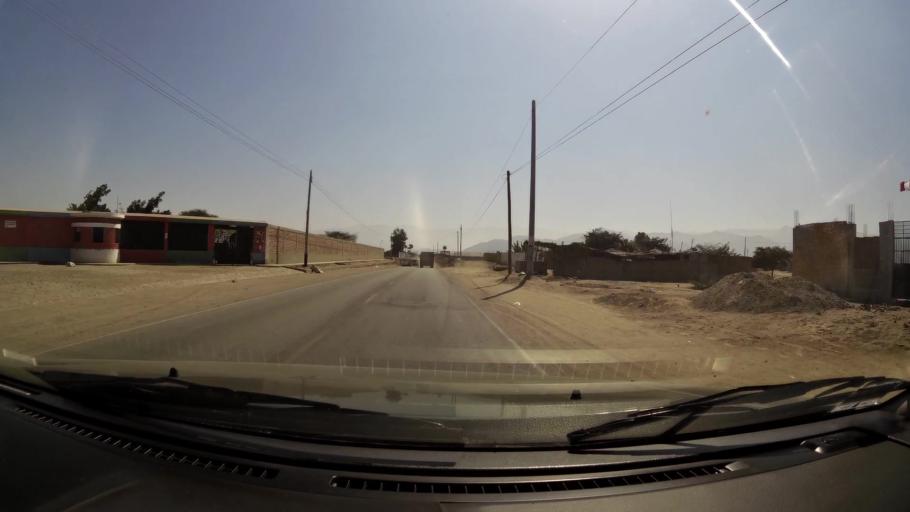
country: PE
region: Ica
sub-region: Provincia de Ica
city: La Tinguina
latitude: -14.0266
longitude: -75.7081
